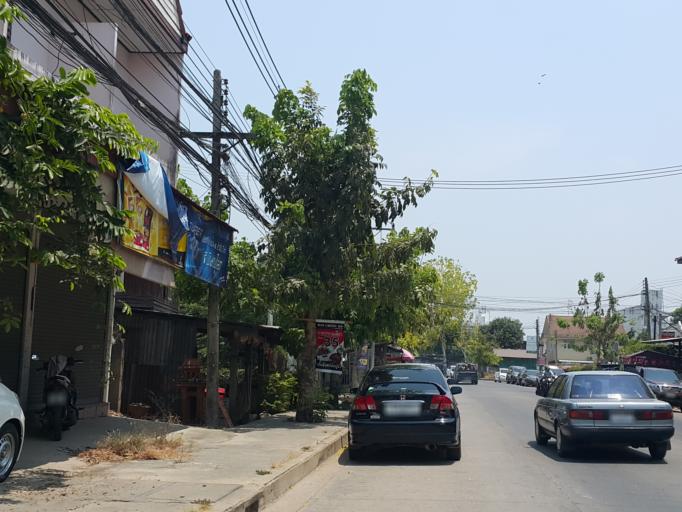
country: TH
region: Phitsanulok
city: Phitsanulok
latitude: 16.8123
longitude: 100.2552
